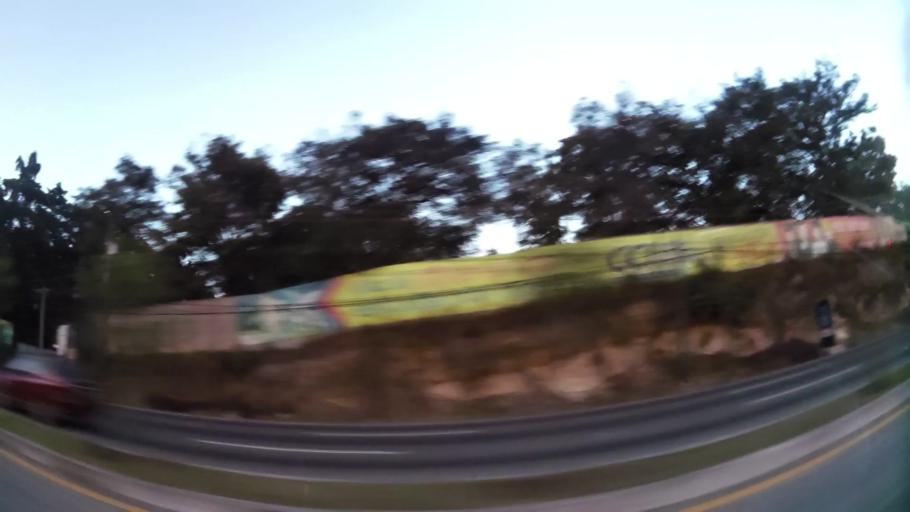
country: GT
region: Guatemala
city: Mixco
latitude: 14.6153
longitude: -90.6186
